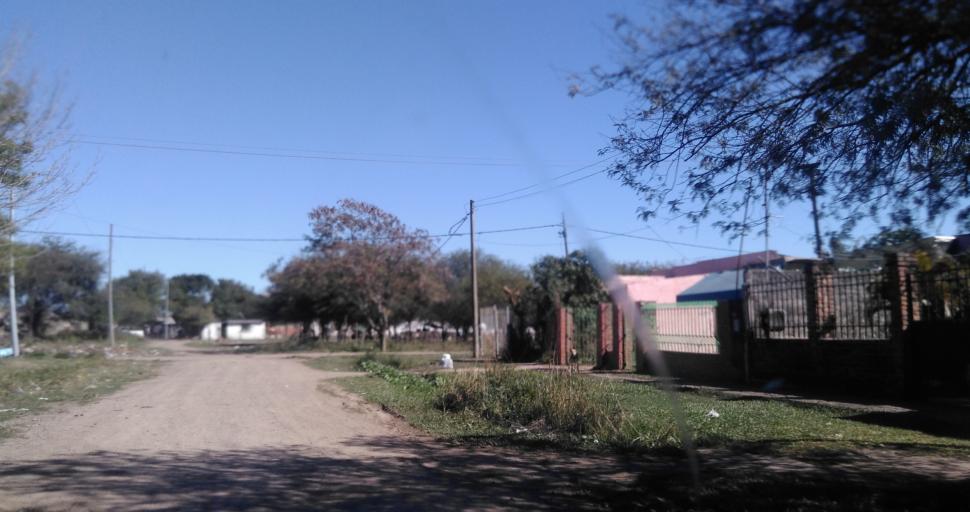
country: AR
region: Chaco
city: Fontana
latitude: -27.4312
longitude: -59.0192
